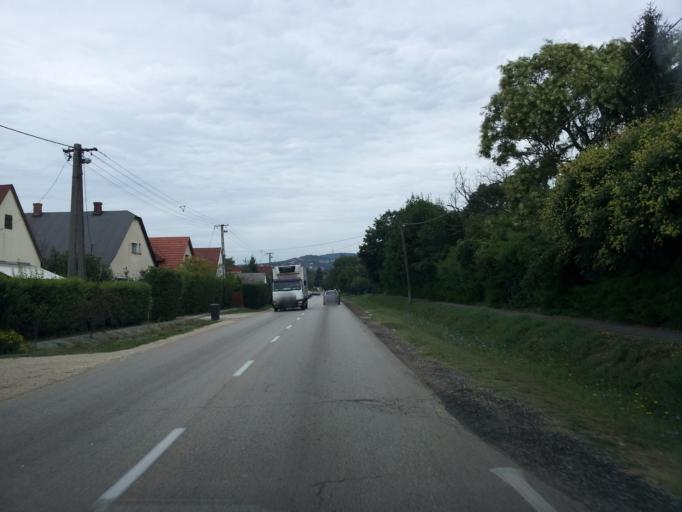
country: HU
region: Fejer
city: Velence
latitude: 47.2398
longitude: 18.6566
